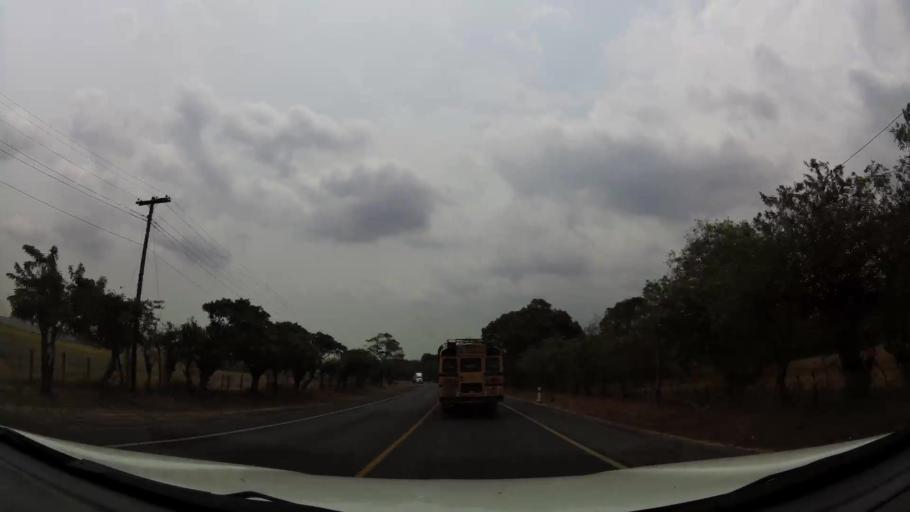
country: NI
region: Leon
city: Telica
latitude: 12.5203
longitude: -86.8674
